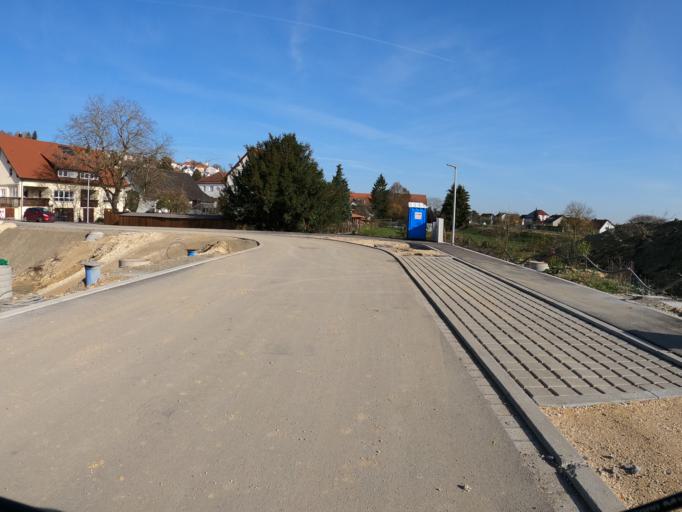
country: DE
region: Bavaria
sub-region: Swabia
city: Nersingen
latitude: 48.4474
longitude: 10.0802
